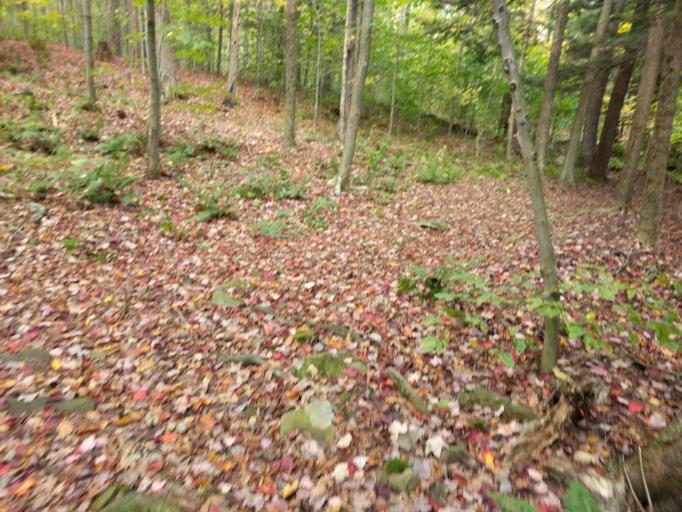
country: US
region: New York
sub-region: Sullivan County
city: Livingston Manor
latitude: 41.8748
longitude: -75.0306
